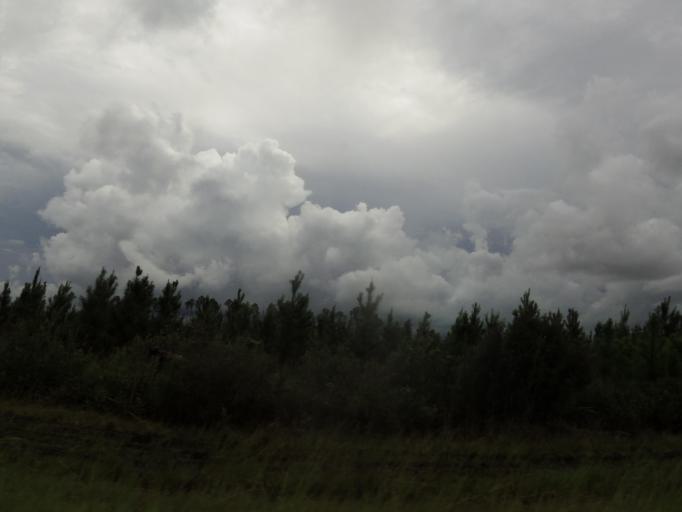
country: US
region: Florida
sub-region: Baker County
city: Macclenny
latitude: 30.5175
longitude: -82.1151
